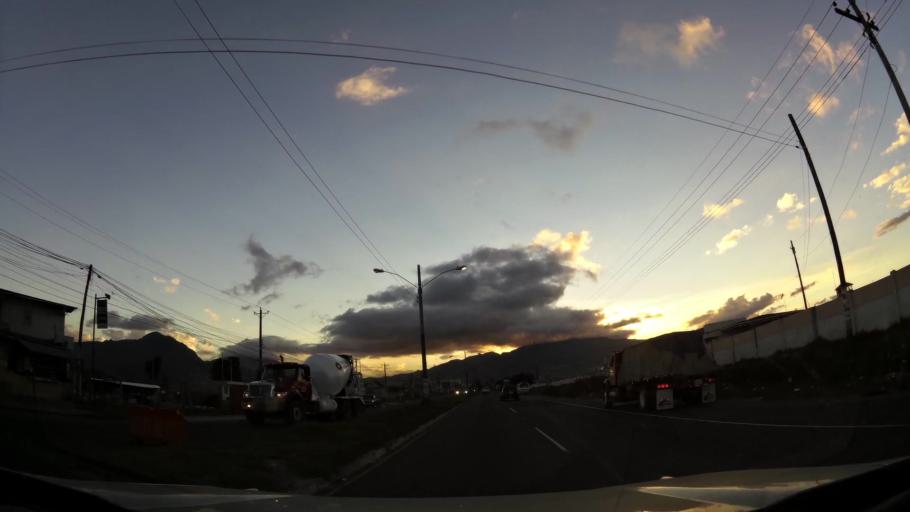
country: GT
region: Quetzaltenango
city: Olintepeque
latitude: 14.8612
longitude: -91.5060
